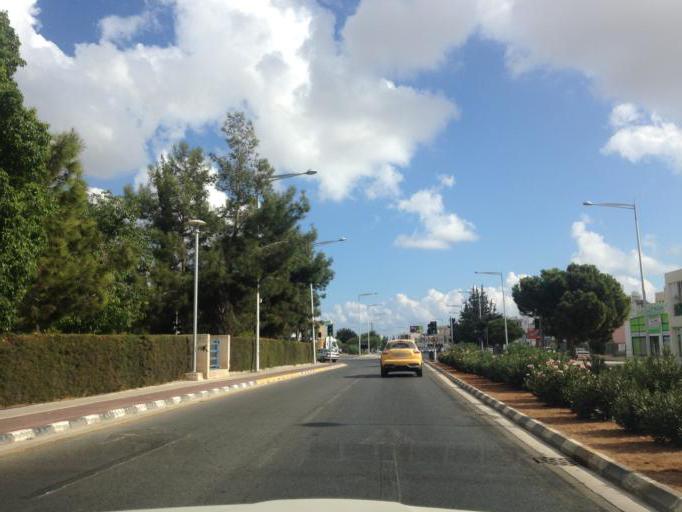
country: CY
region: Pafos
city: Paphos
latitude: 34.7660
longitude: 32.4454
